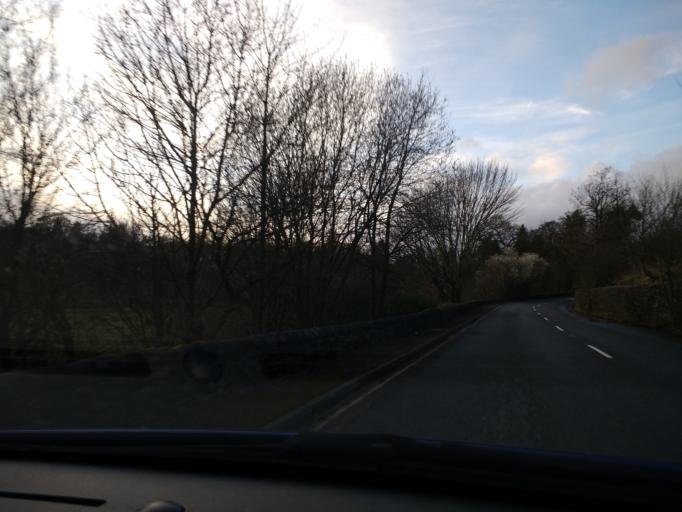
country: GB
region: England
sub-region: North Yorkshire
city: Settle
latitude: 54.0740
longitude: -2.2902
